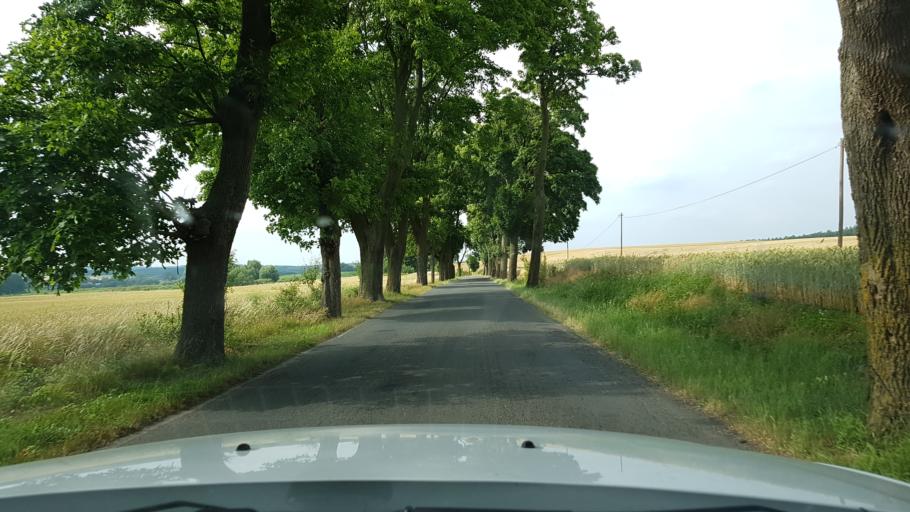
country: PL
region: West Pomeranian Voivodeship
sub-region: Powiat gryfinski
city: Moryn
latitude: 52.9037
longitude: 14.3742
